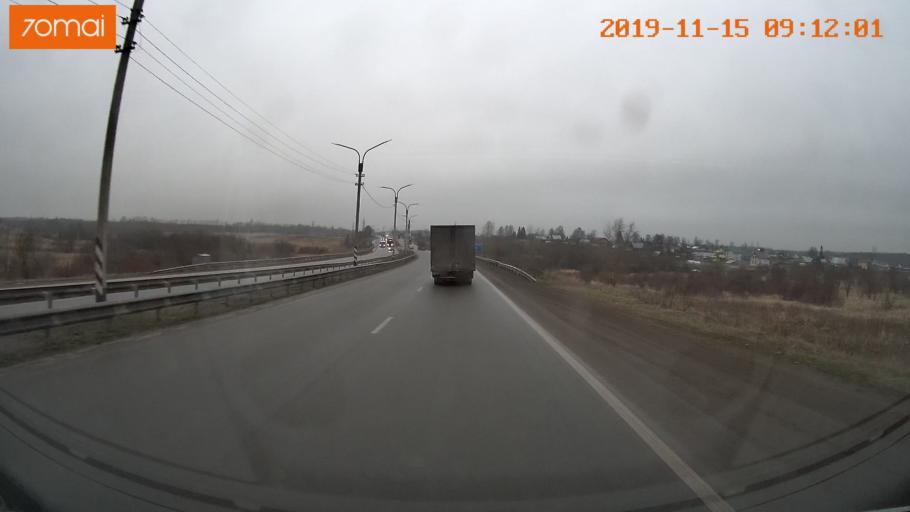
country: RU
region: Vologda
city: Tonshalovo
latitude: 59.2039
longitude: 37.9414
